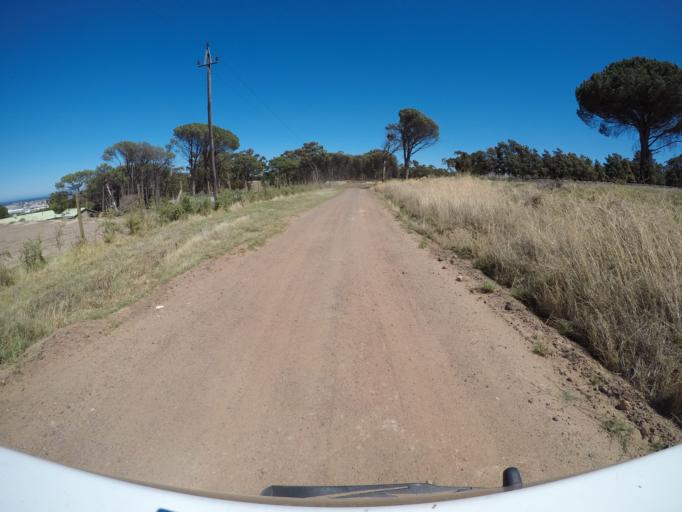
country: ZA
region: Western Cape
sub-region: Overberg District Municipality
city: Grabouw
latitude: -34.1154
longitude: 18.8805
